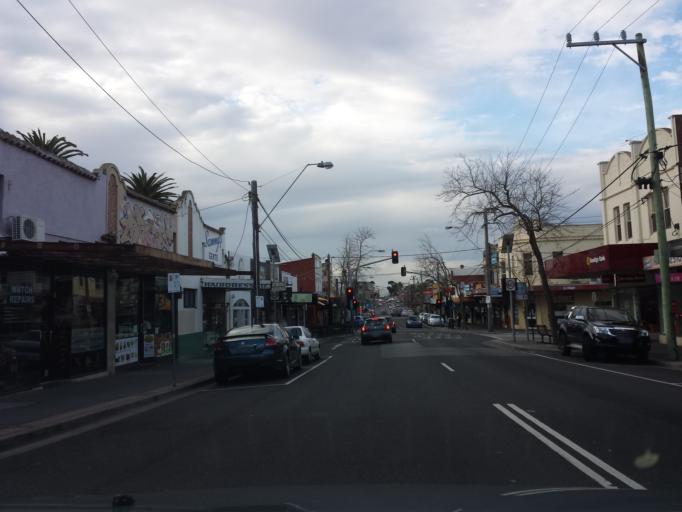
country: AU
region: Victoria
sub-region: Bayside
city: Cheltenham
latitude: -37.9674
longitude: 145.0552
